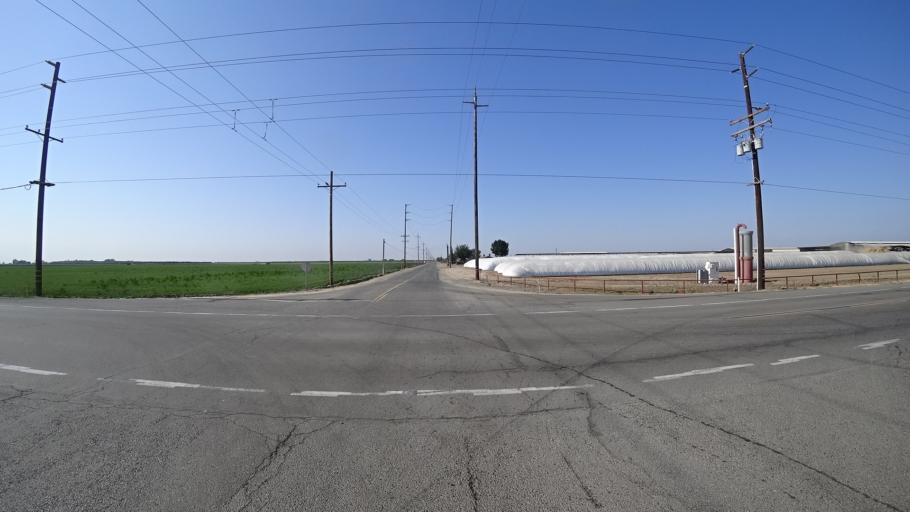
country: US
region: California
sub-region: Kings County
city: Home Garden
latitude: 36.2986
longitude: -119.5831
